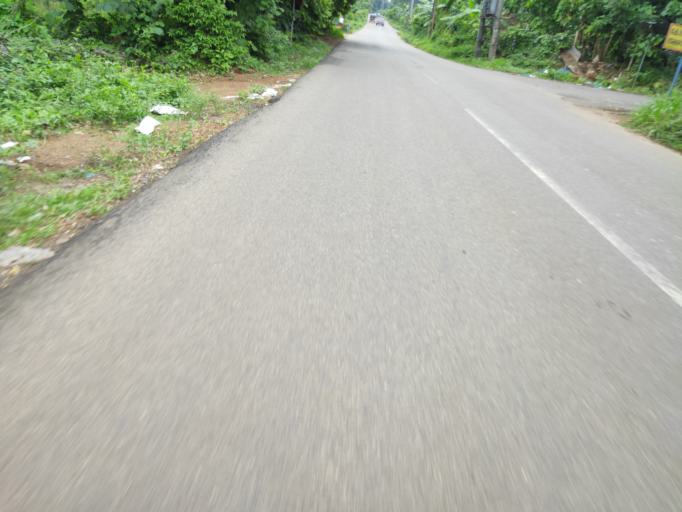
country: IN
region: Kerala
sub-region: Malappuram
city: Manjeri
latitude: 11.2243
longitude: 76.2654
